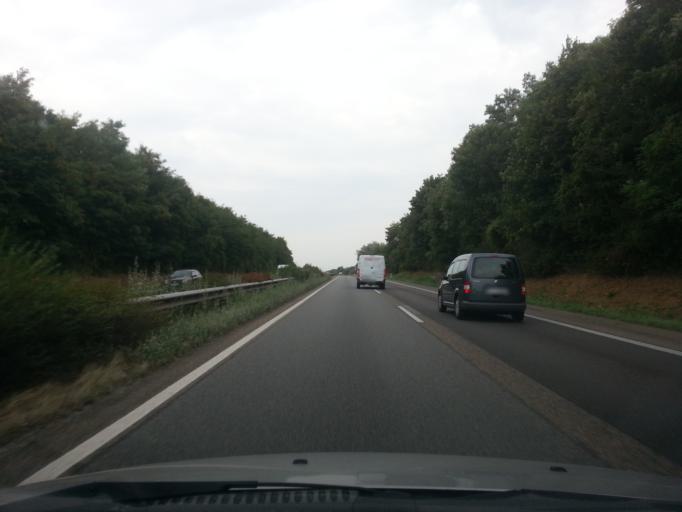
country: DE
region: Rheinland-Pfalz
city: Knoringen
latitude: 49.2494
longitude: 8.1494
